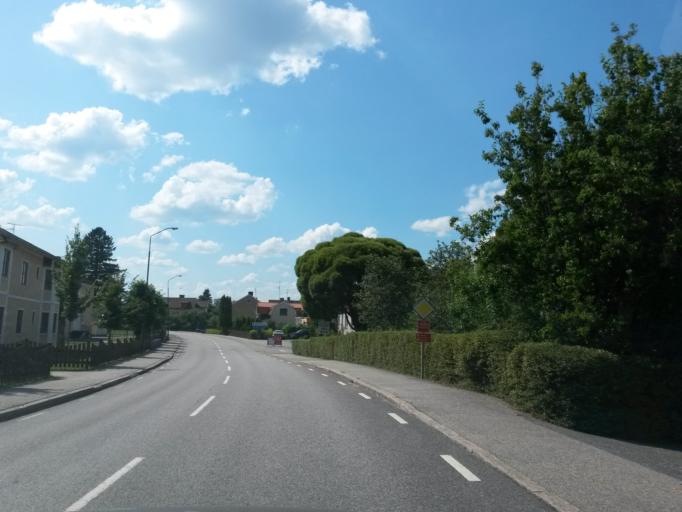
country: SE
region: Vaestra Goetaland
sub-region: Herrljunga Kommun
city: Herrljunga
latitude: 58.0799
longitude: 13.0340
